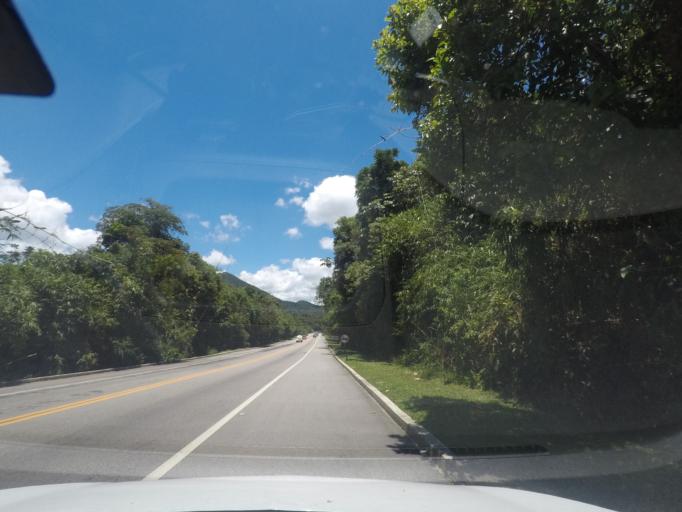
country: BR
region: Rio de Janeiro
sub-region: Teresopolis
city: Teresopolis
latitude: -22.4605
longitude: -42.9805
